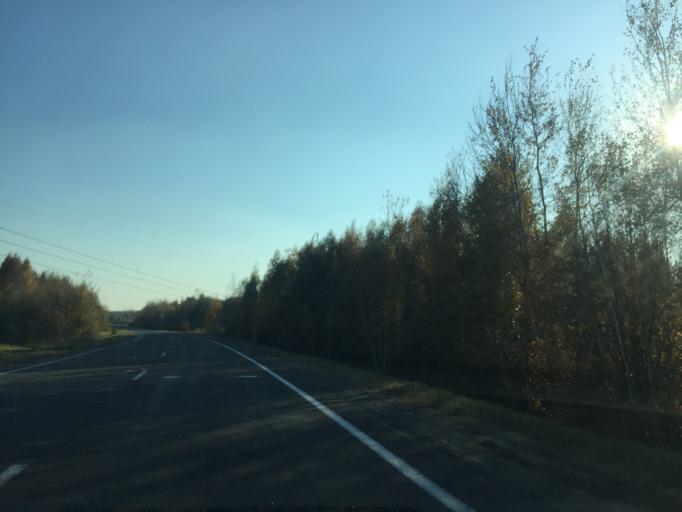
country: BY
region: Gomel
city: Dobrush
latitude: 52.3510
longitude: 31.2292
